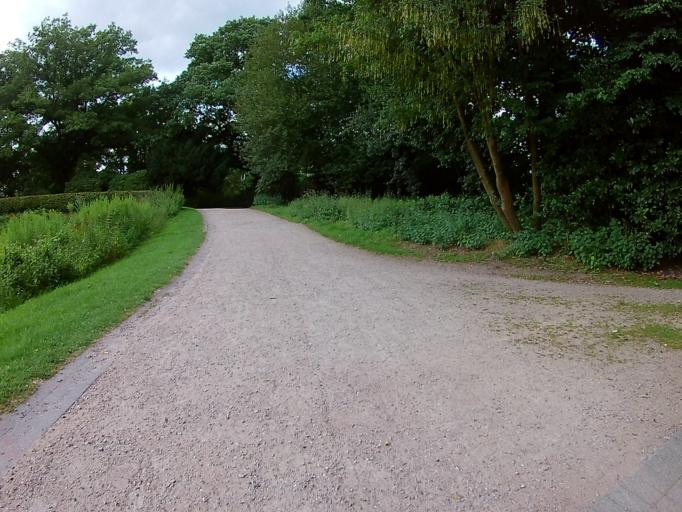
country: DE
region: Hamburg
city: Harburg
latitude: 53.4466
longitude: 9.9705
